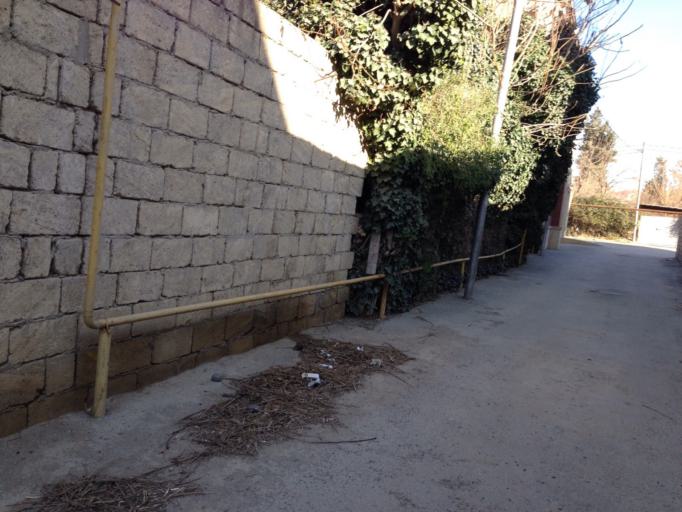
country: AZ
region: Baki
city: Baku
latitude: 40.3900
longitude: 49.8776
